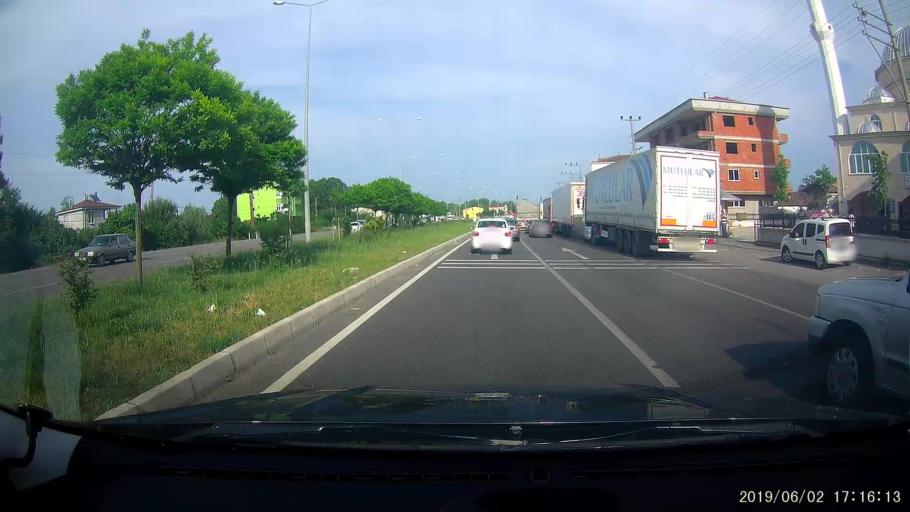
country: TR
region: Samsun
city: Dikbiyik
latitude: 41.2342
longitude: 36.5665
